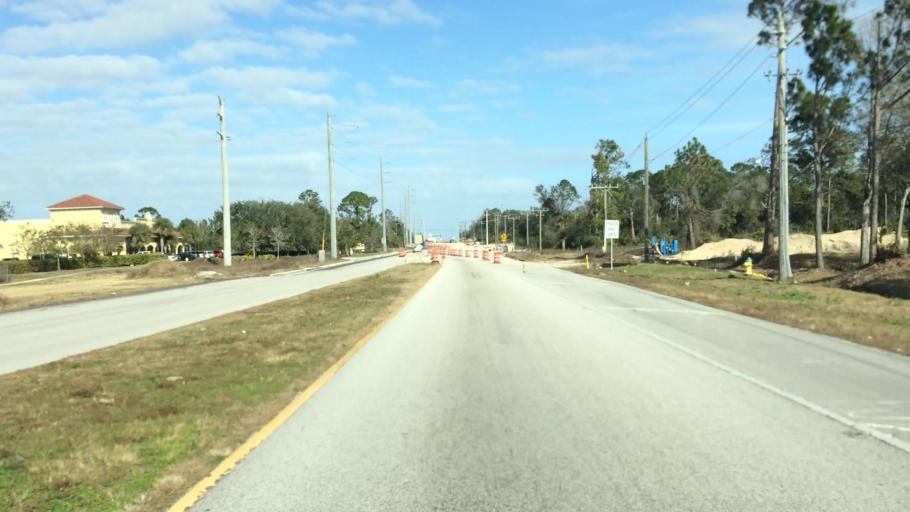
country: US
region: Florida
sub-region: Volusia County
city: Holly Hill
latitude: 29.2325
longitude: -81.0730
